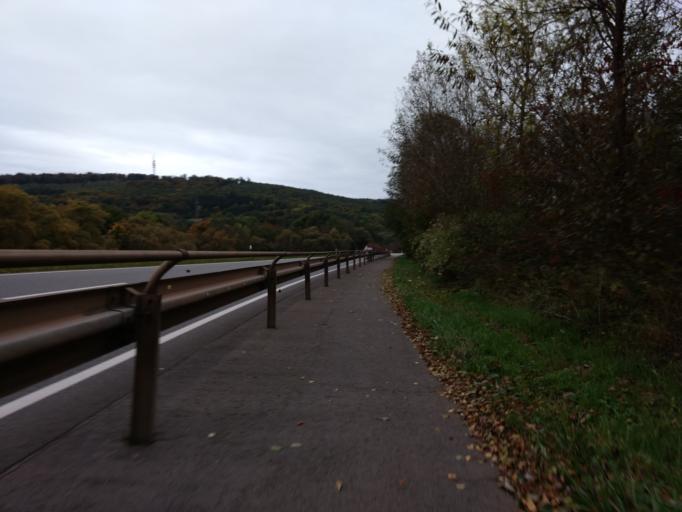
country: DE
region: Saarland
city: Schmelz
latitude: 49.4002
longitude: 6.8488
